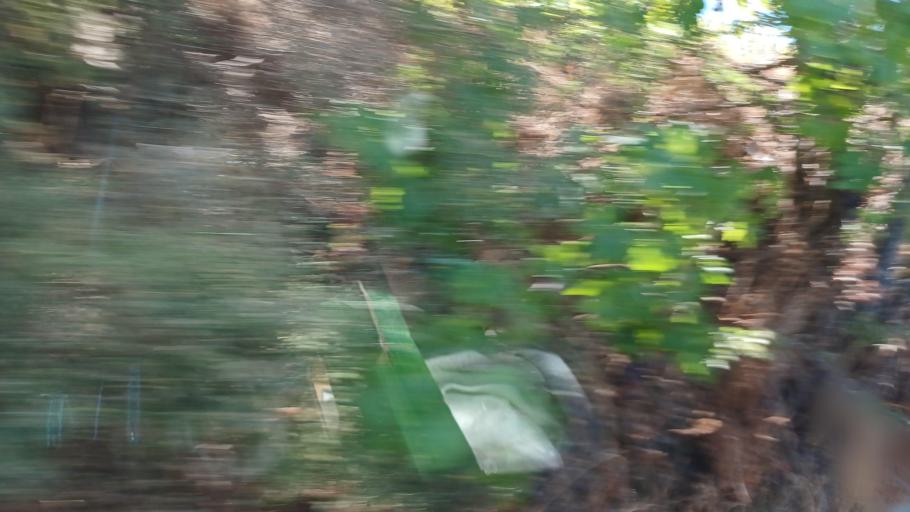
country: CY
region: Pafos
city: Mesogi
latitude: 34.9251
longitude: 32.6368
